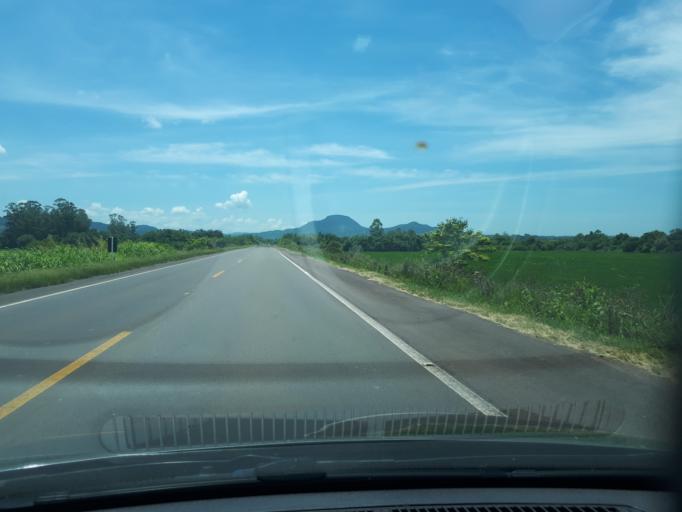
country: BR
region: Rio Grande do Sul
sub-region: Candelaria
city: Candelaria
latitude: -29.7286
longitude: -52.9389
